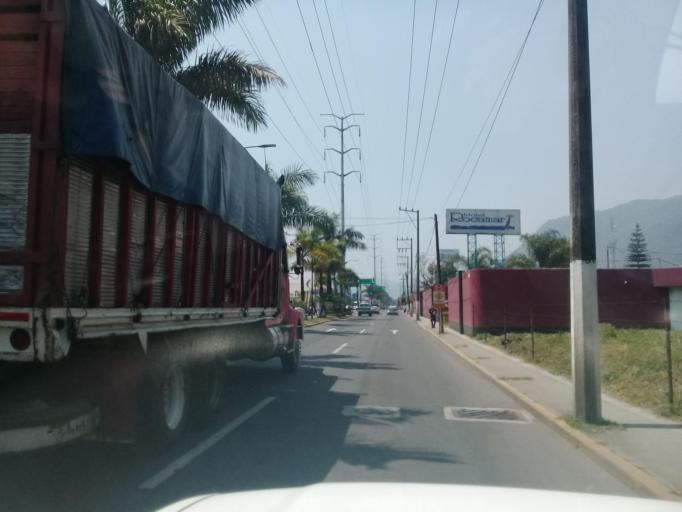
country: MX
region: Veracruz
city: Ixtac Zoquitlan
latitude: 18.8610
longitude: -97.0602
